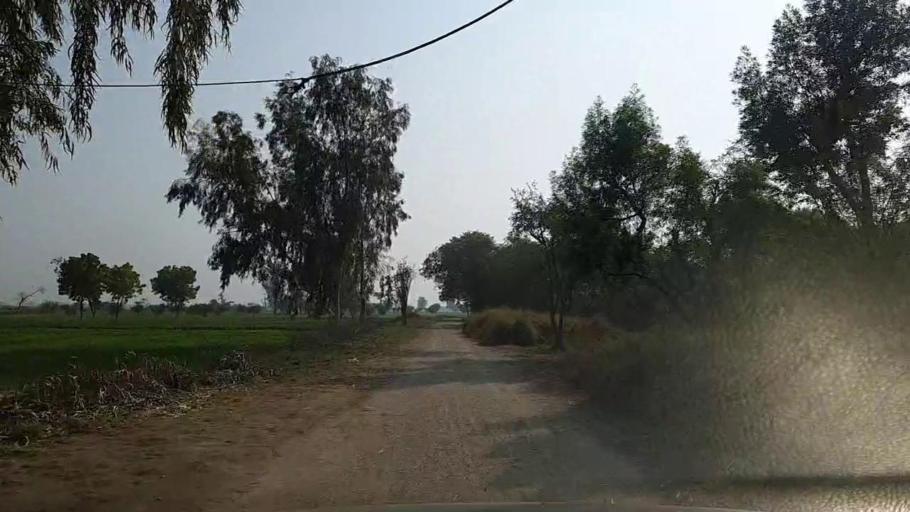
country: PK
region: Sindh
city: Nawabshah
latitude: 26.2768
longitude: 68.4392
